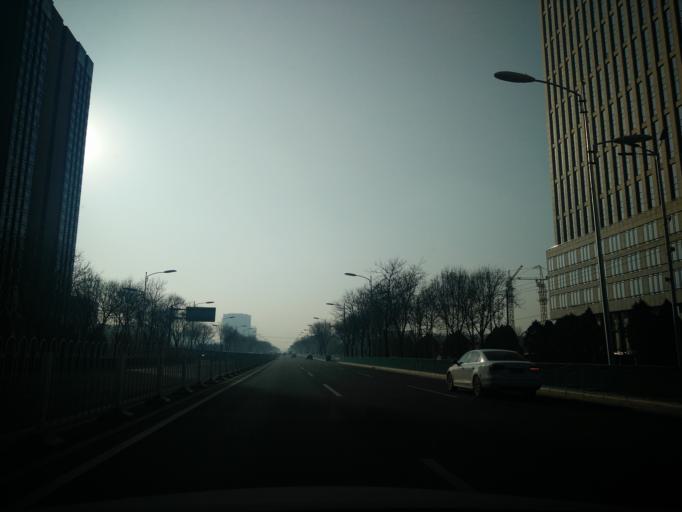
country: CN
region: Beijing
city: Jiugong
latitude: 39.7907
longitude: 116.5018
